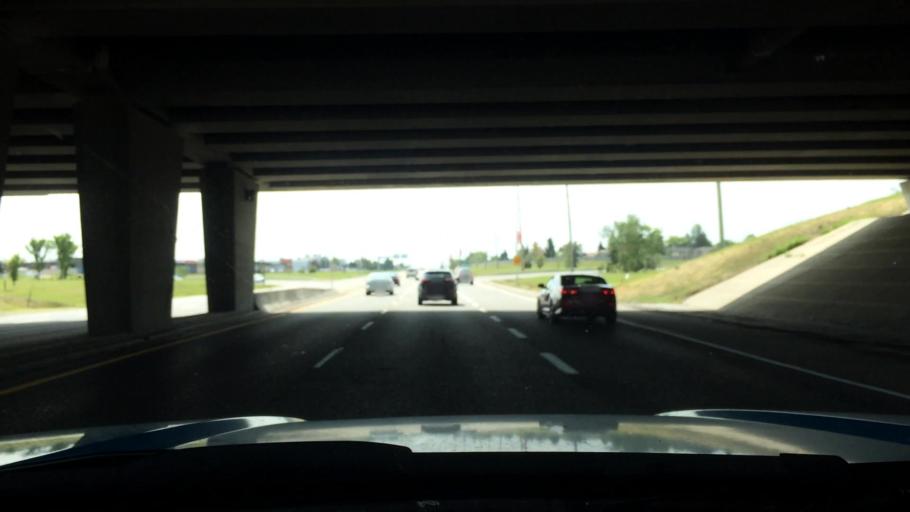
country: CA
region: Alberta
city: Calgary
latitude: 51.0671
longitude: -114.0019
